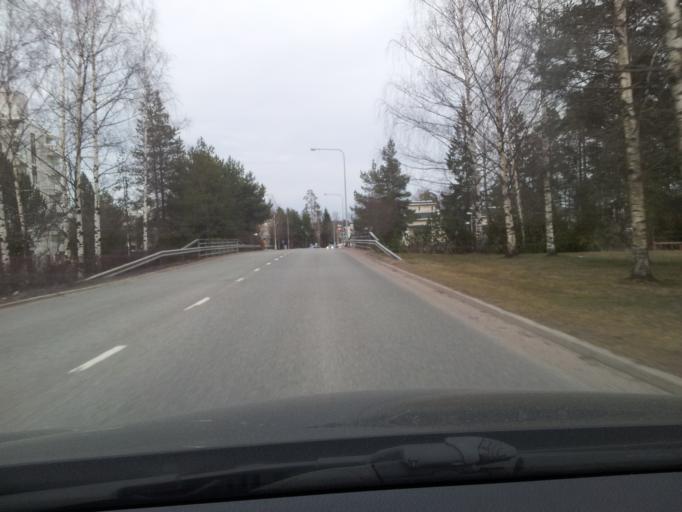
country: FI
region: Uusimaa
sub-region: Helsinki
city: Espoo
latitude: 60.1472
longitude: 24.6572
